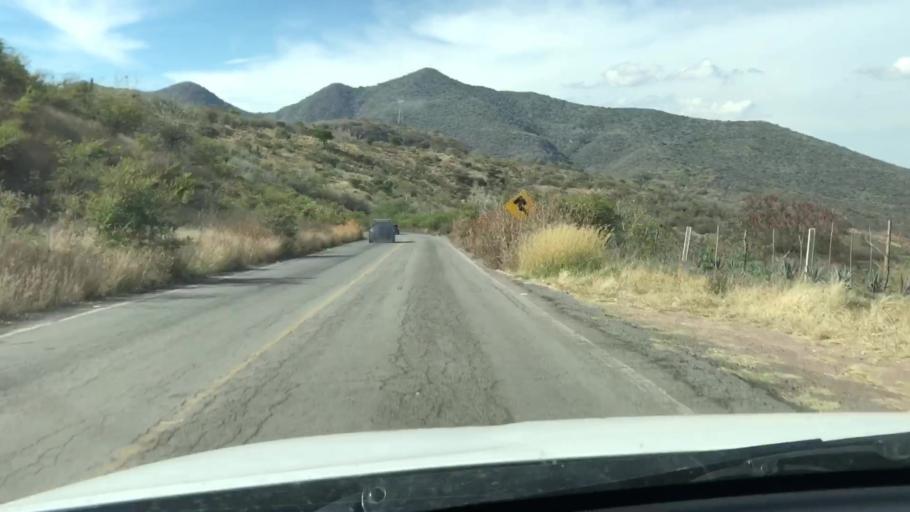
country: MX
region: Jalisco
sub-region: Zacoalco de Torres
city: Barranca de Otates (Barranca de Otatan)
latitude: 20.2514
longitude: -103.6713
